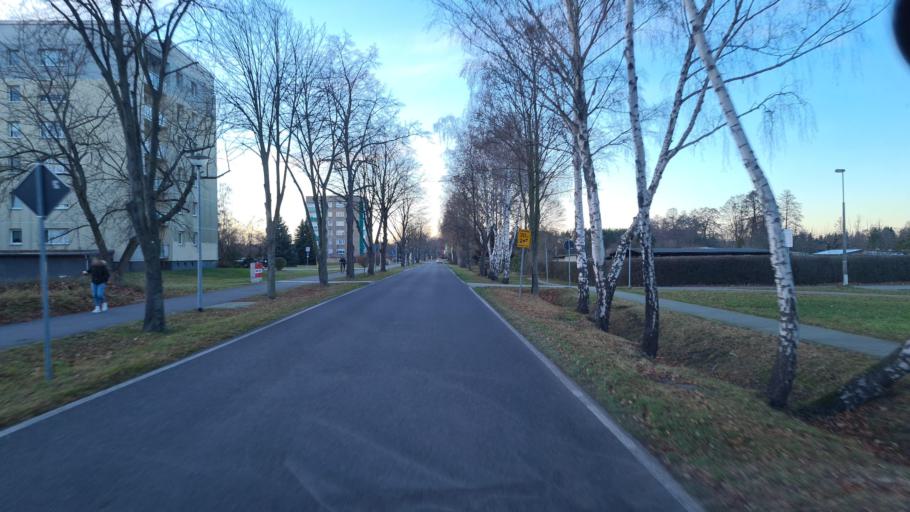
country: DE
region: Brandenburg
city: Vetschau
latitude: 51.7796
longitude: 14.0826
